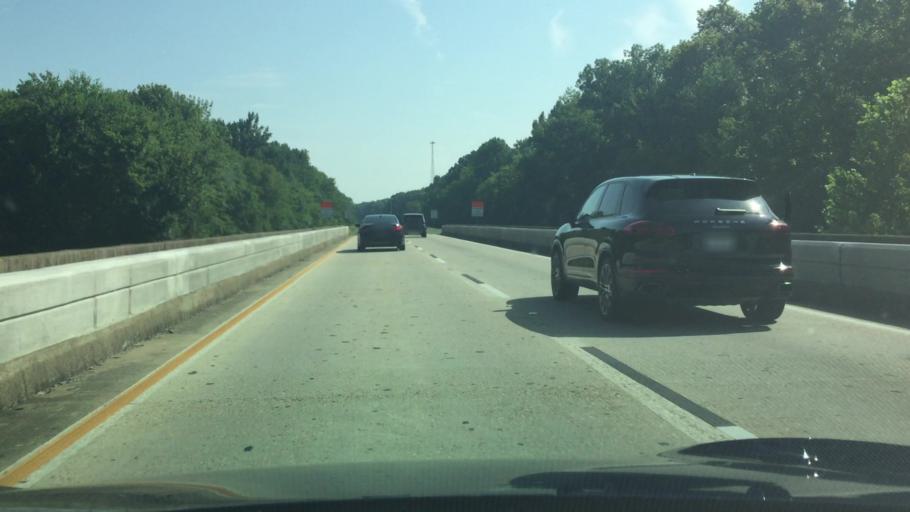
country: US
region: Alabama
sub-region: Montgomery County
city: Montgomery
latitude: 32.2266
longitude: -86.3892
